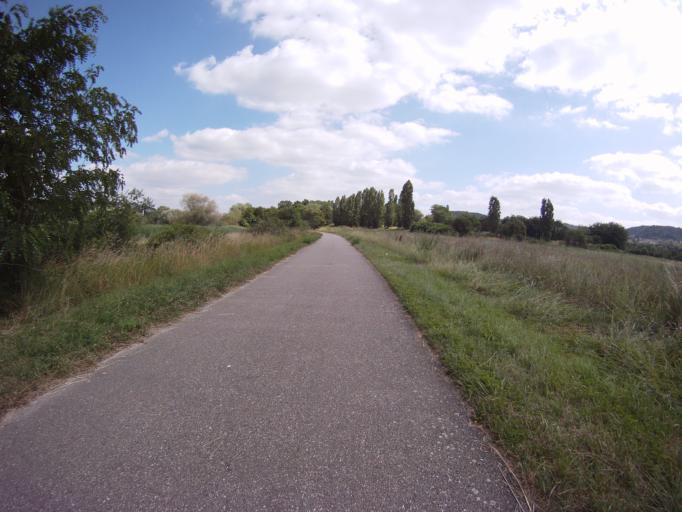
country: FR
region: Lorraine
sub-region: Departement de Meurthe-et-Moselle
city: Frouard
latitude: 48.7647
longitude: 6.1410
